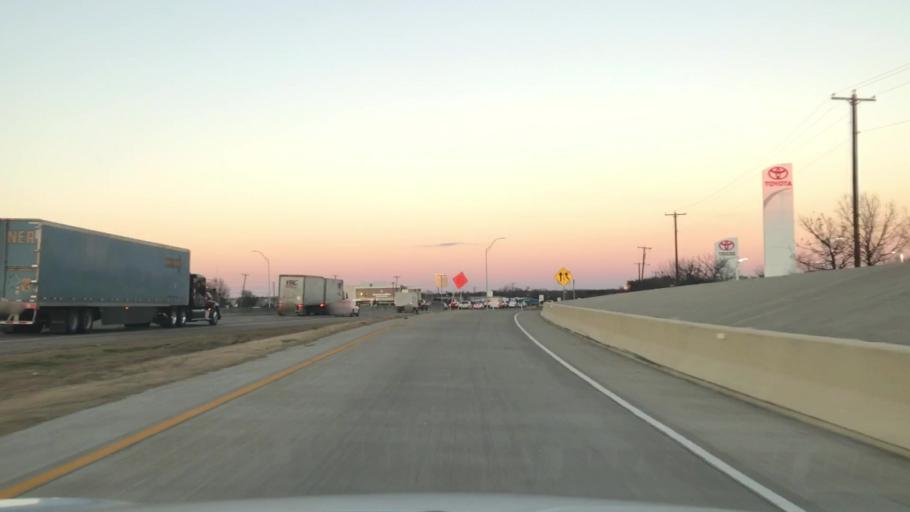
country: US
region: Texas
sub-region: Rockwall County
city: Rockwall
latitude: 32.9114
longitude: -96.4476
